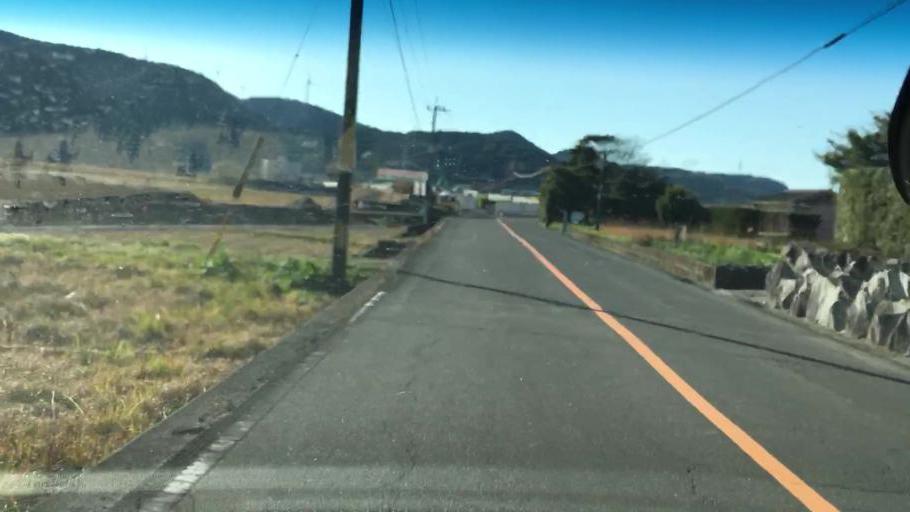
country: JP
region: Kagoshima
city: Satsumasendai
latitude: 31.8295
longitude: 130.2405
